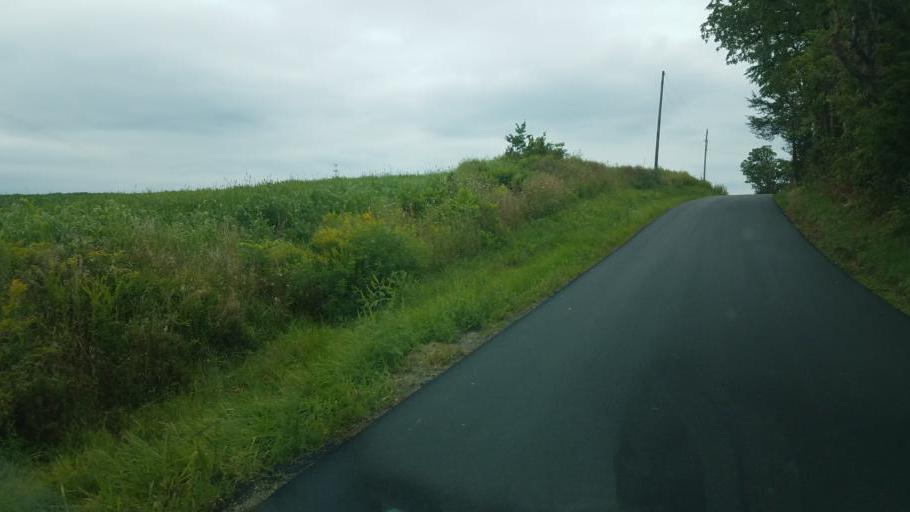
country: US
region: Ohio
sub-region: Morrow County
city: Mount Gilead
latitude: 40.5535
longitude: -82.7720
